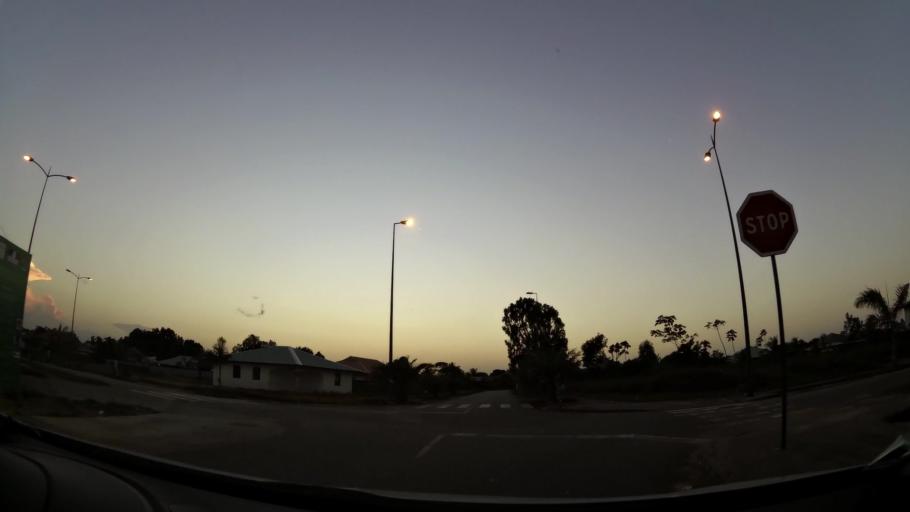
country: GF
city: Macouria
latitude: 4.9279
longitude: -52.4122
